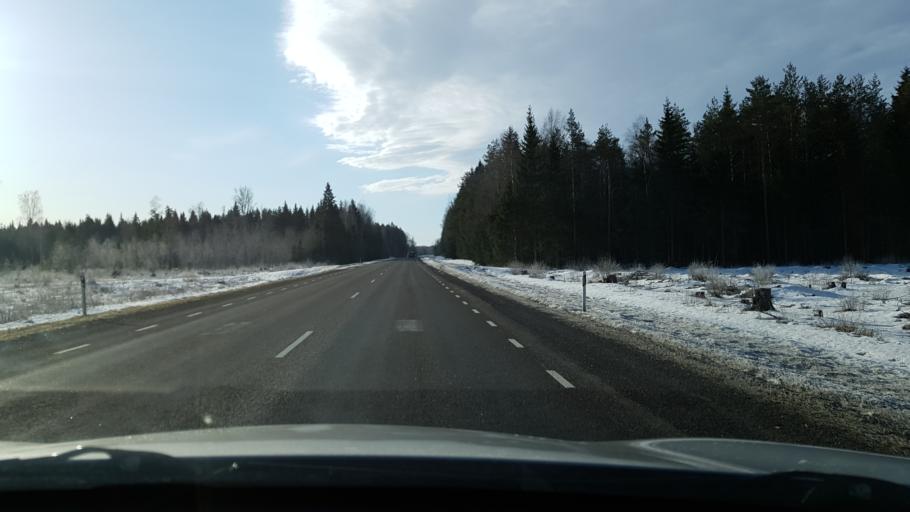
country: EE
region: Viljandimaa
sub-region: Vohma linn
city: Vohma
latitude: 58.5966
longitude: 25.5722
